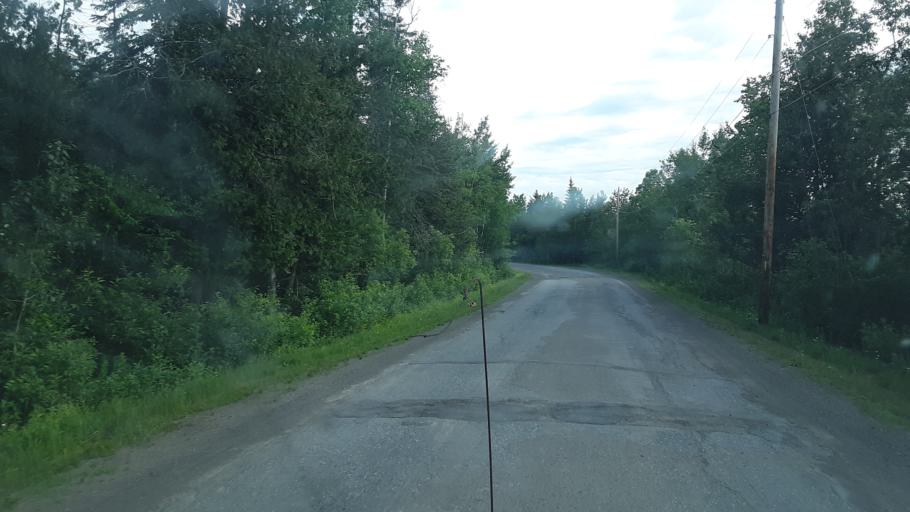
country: US
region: Maine
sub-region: Aroostook County
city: Caribou
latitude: 46.8444
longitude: -68.0921
